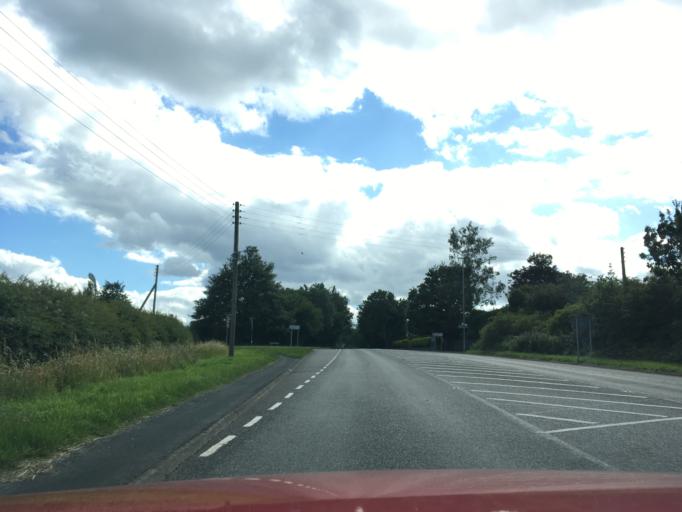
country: GB
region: England
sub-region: Leicestershire
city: Coalville
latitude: 52.7606
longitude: -1.4047
